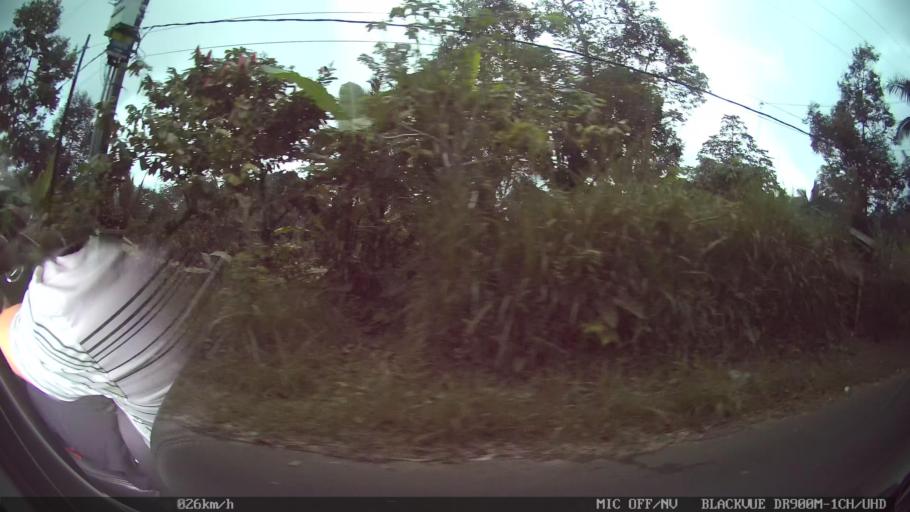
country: ID
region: Bali
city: Peneng
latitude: -8.3683
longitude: 115.2174
